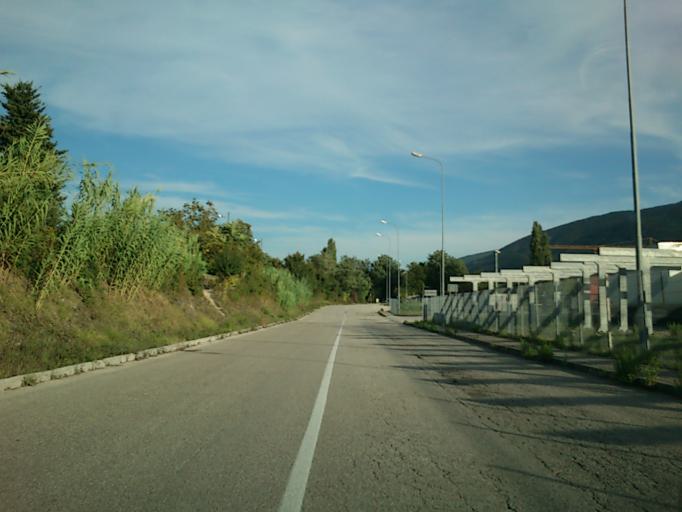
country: IT
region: The Marches
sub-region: Provincia di Pesaro e Urbino
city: Canavaccio
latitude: 43.6962
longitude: 12.6944
